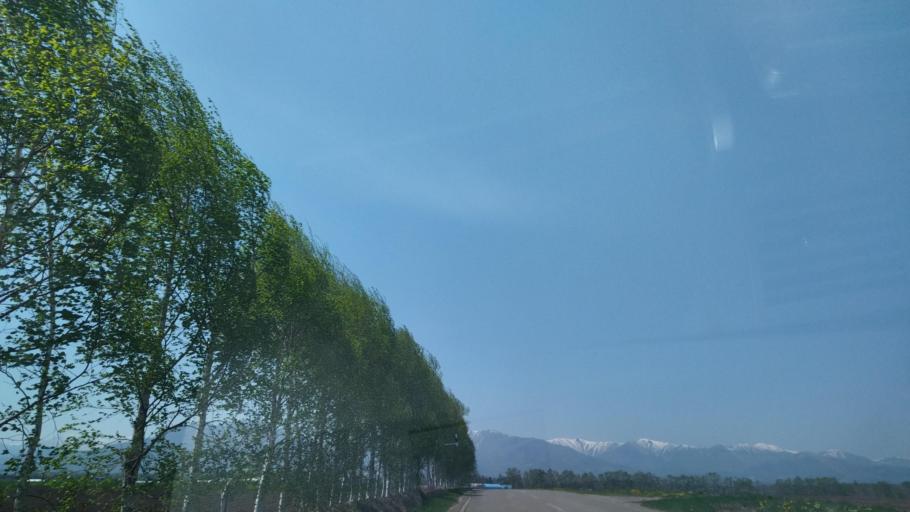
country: JP
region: Hokkaido
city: Obihiro
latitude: 42.8933
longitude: 143.0156
